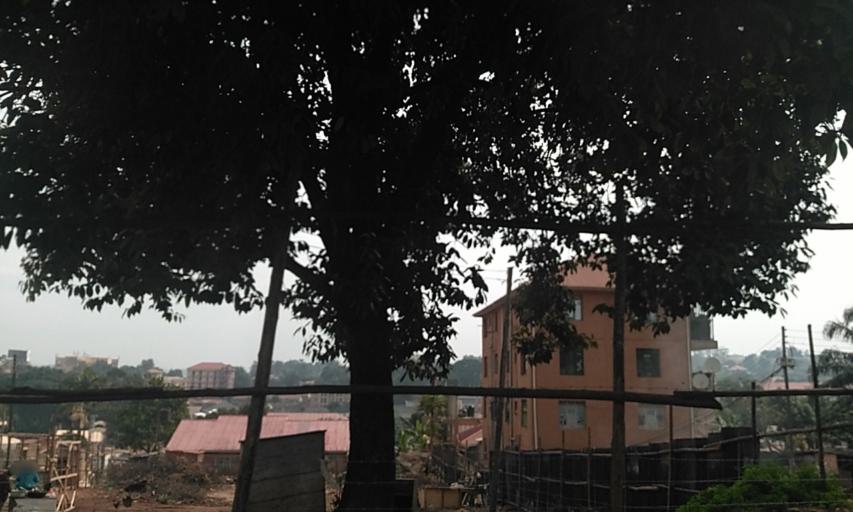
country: UG
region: Central Region
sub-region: Kampala District
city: Kampala
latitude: 0.3022
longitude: 32.5585
